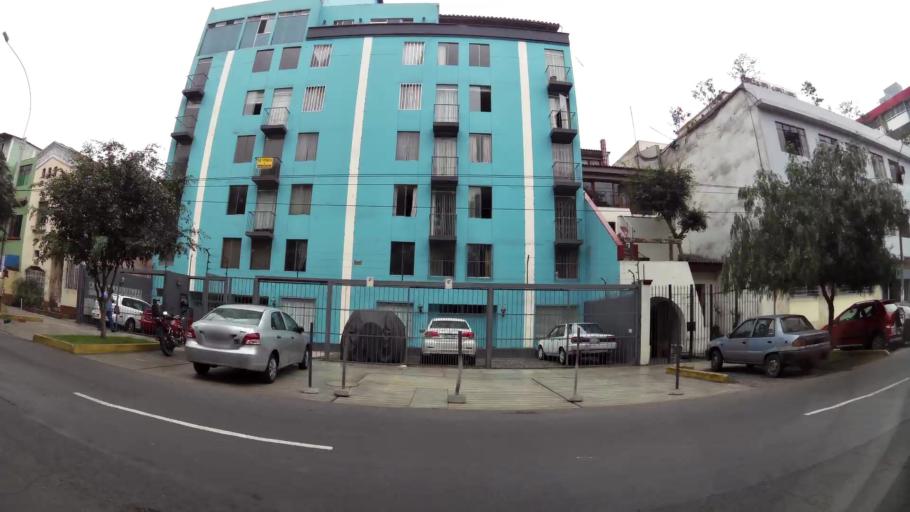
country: PE
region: Lima
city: Lima
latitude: -12.0732
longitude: -77.0347
